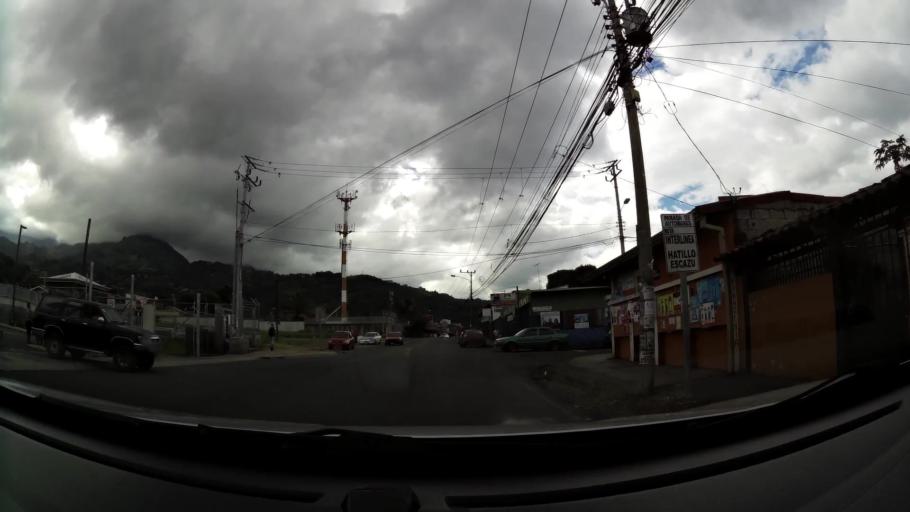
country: CR
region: San Jose
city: San Felipe
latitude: 9.9034
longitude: -84.1032
